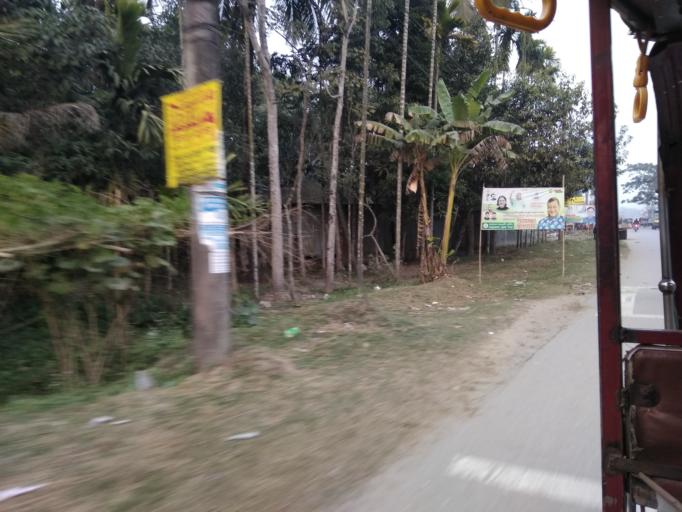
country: BD
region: Dhaka
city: Netrakona
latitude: 24.8696
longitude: 90.7099
